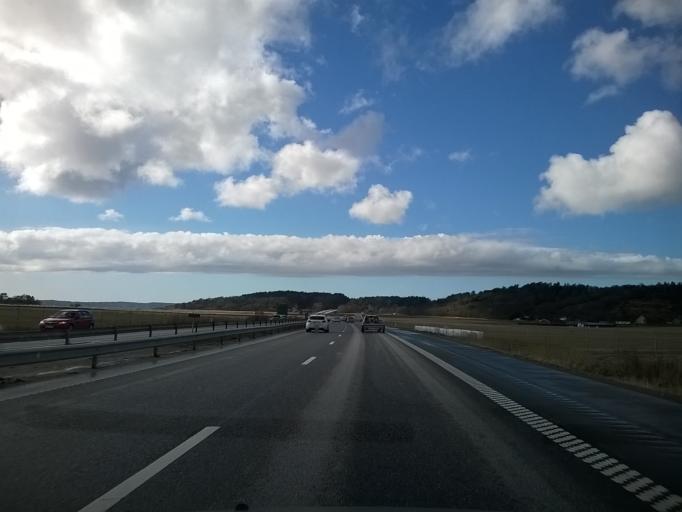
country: SE
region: Halland
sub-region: Kungsbacka Kommun
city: Fjaeras kyrkby
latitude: 57.4347
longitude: 12.1463
